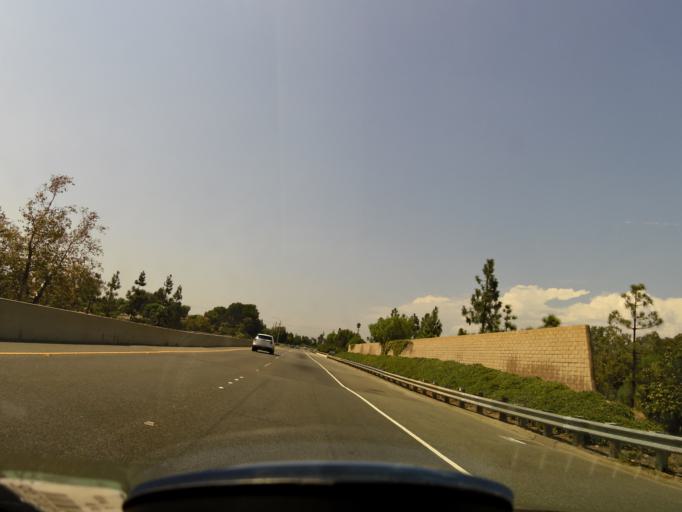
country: US
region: California
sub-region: Orange County
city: Yorba Linda
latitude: 33.8730
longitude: -117.8018
